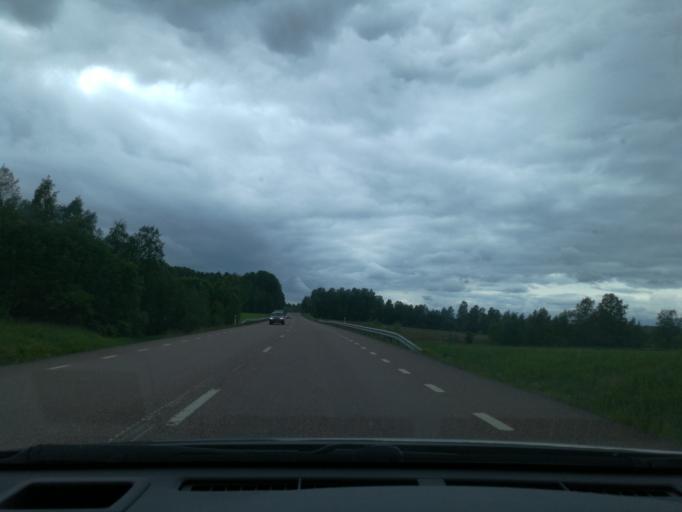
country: SE
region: Dalarna
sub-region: Smedjebackens Kommun
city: Smedjebacken
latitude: 60.1396
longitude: 15.3794
